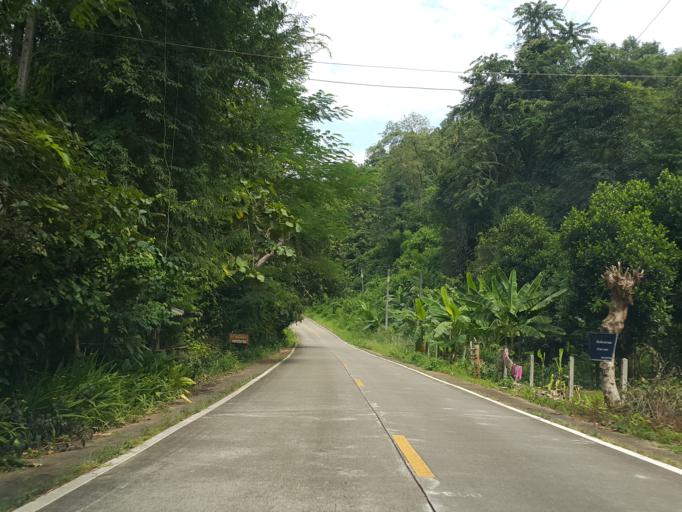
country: TH
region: Mae Hong Son
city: Mae Hong Son
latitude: 19.4556
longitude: 97.9667
